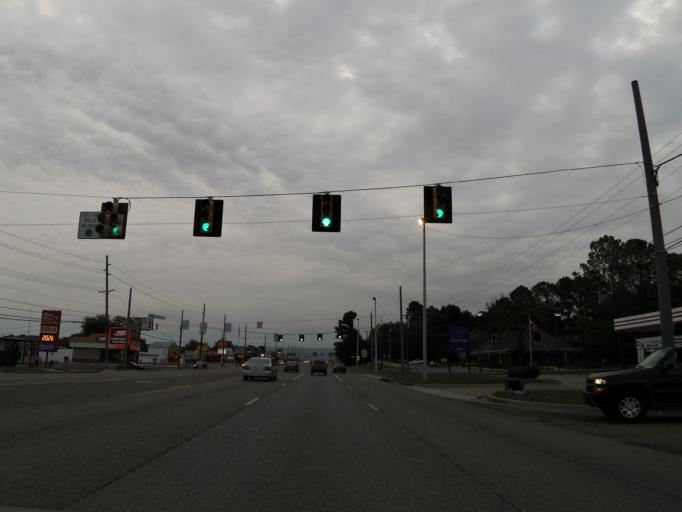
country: US
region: Alabama
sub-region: Madison County
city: Huntsville
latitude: 34.7350
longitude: -86.6340
